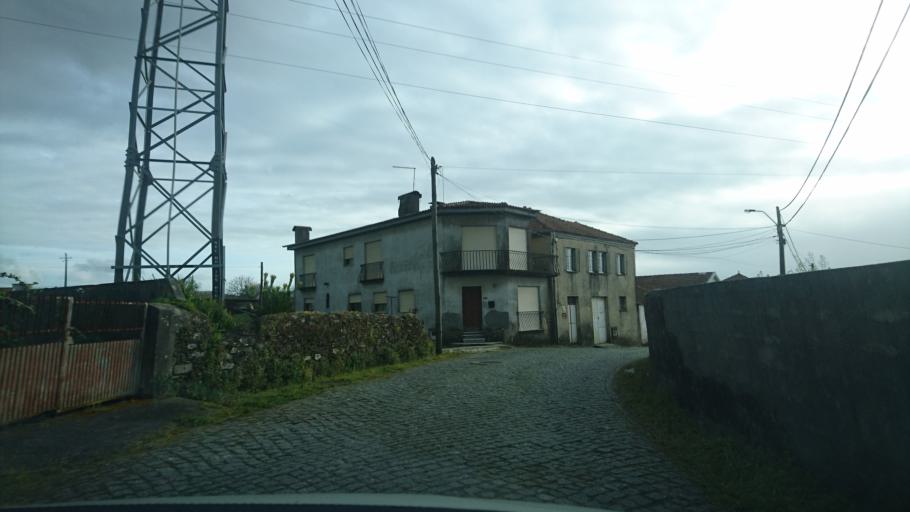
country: PT
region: Aveiro
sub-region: Ovar
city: Cortegaca
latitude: 40.9583
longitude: -8.6168
